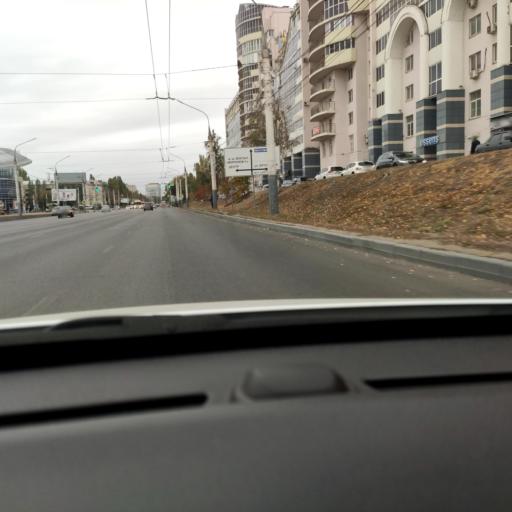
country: RU
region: Voronezj
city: Voronezh
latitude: 51.6623
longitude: 39.2475
